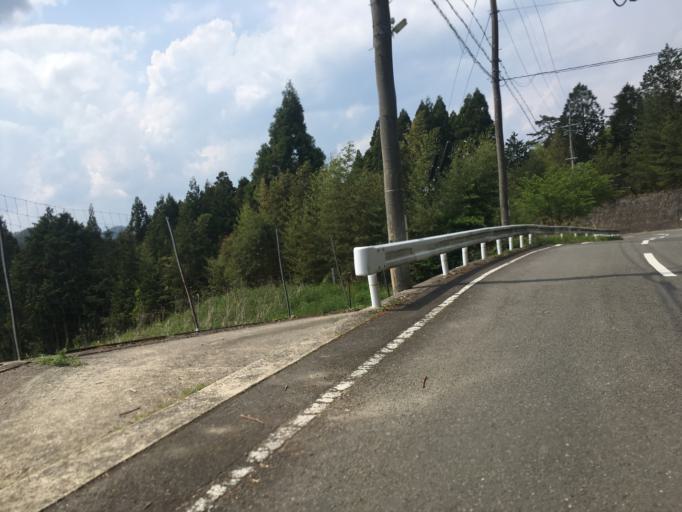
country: JP
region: Kyoto
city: Kameoka
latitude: 35.0793
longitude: 135.6111
